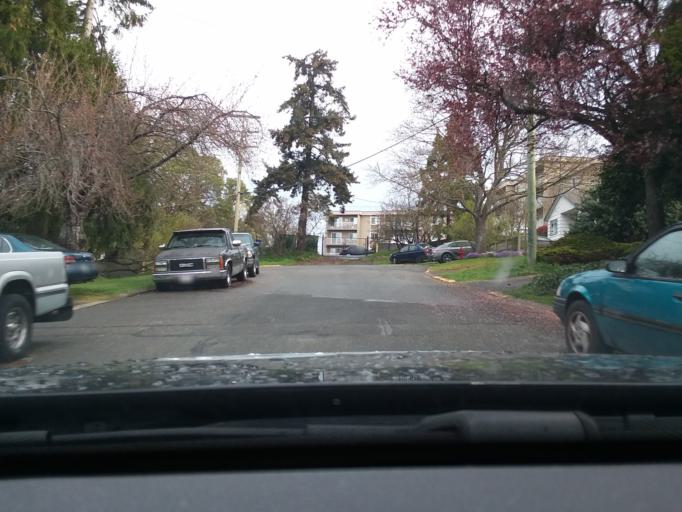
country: CA
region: British Columbia
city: Victoria
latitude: 48.4396
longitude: -123.3991
